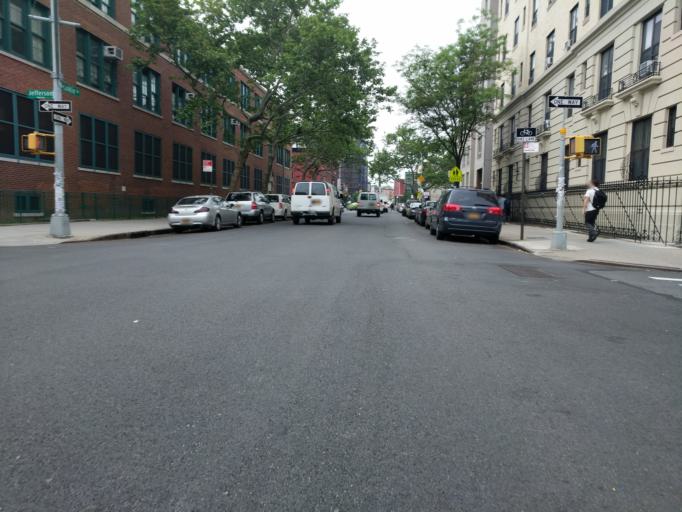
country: US
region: New York
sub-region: Kings County
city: Brooklyn
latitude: 40.6826
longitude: -73.9560
